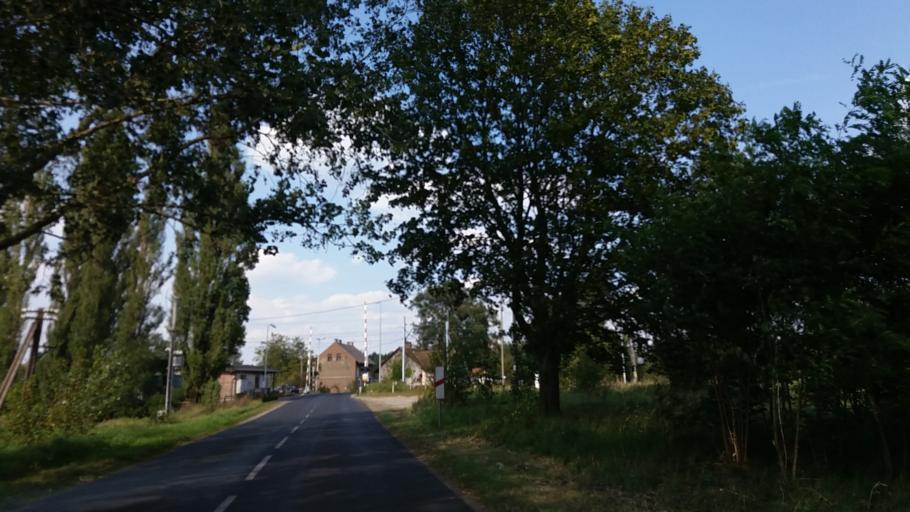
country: PL
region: West Pomeranian Voivodeship
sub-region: Powiat choszczenski
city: Choszczno
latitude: 53.1310
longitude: 15.4547
